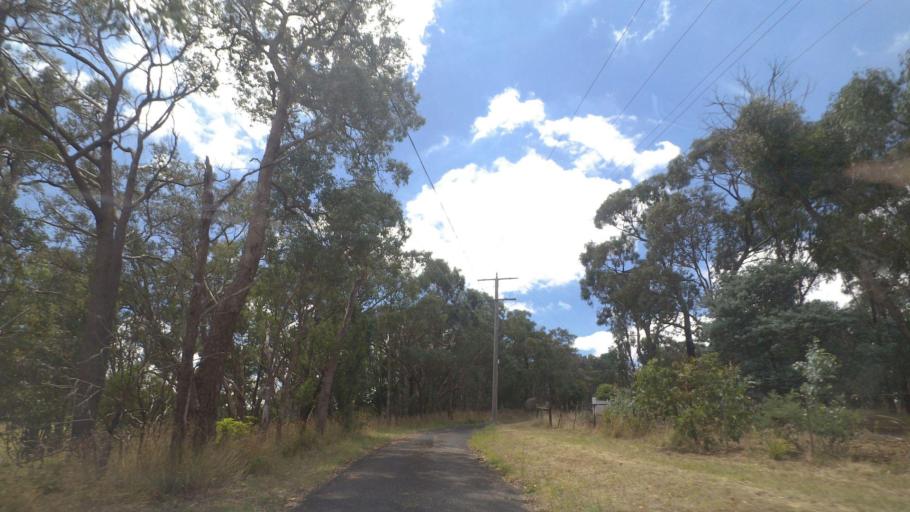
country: AU
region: Victoria
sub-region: Manningham
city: Warrandyte
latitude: -37.7452
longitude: 145.2637
